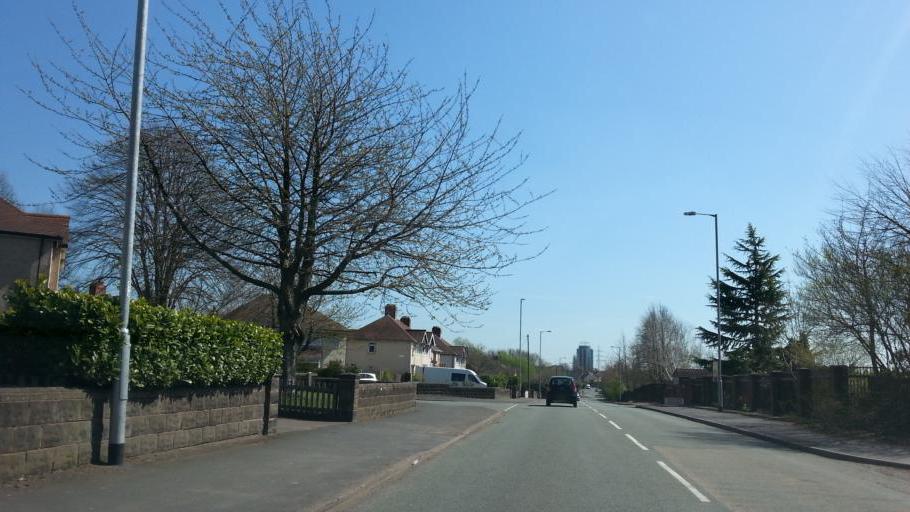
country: GB
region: England
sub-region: Staffordshire
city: Cannock
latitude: 52.6805
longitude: -2.0354
